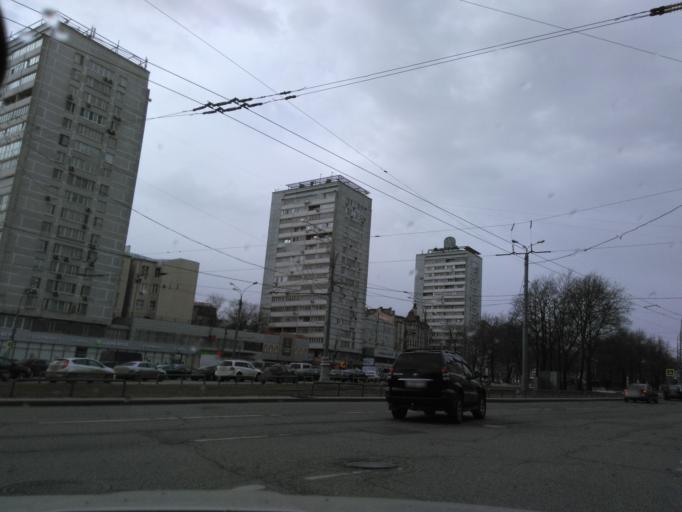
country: RU
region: Moscow
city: Moscow
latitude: 55.7727
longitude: 37.6043
